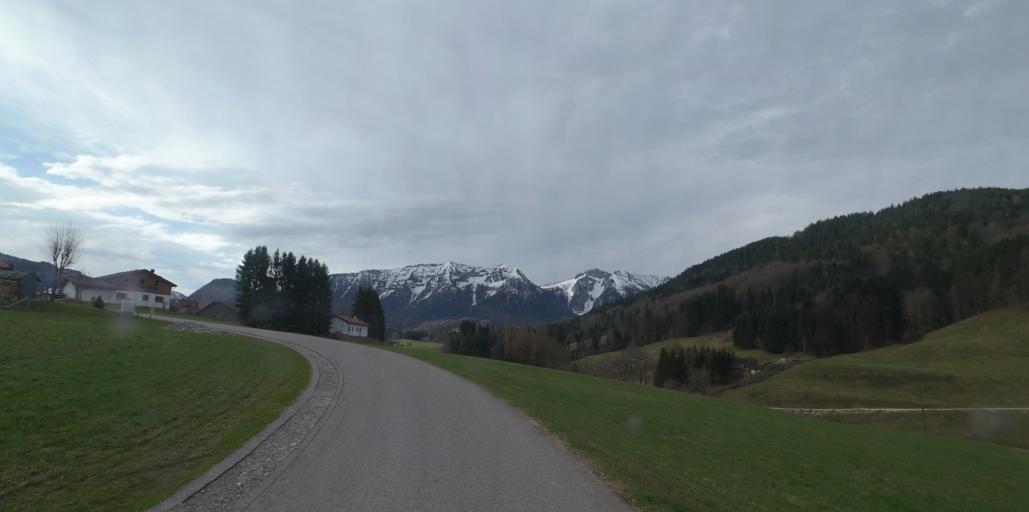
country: DE
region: Bavaria
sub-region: Upper Bavaria
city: Inzell
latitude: 47.7790
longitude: 12.7249
